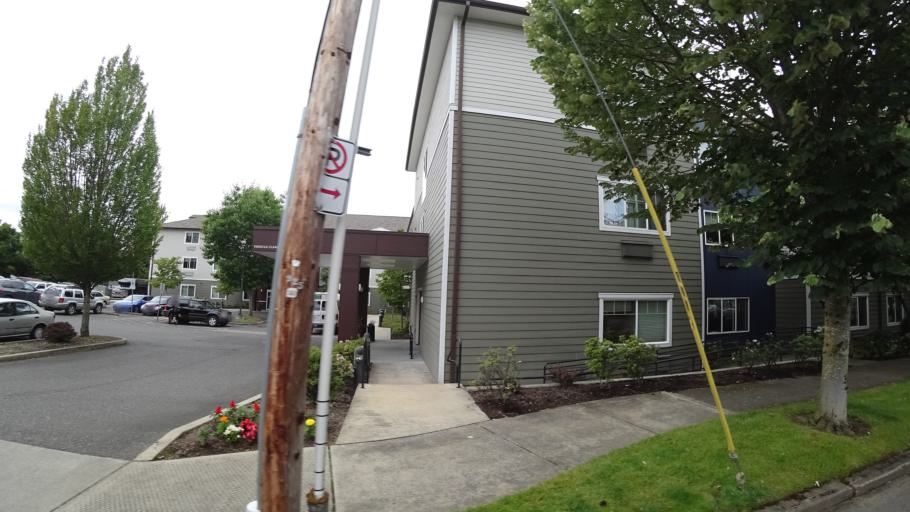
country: US
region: Oregon
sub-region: Multnomah County
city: Portland
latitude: 45.5780
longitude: -122.6630
